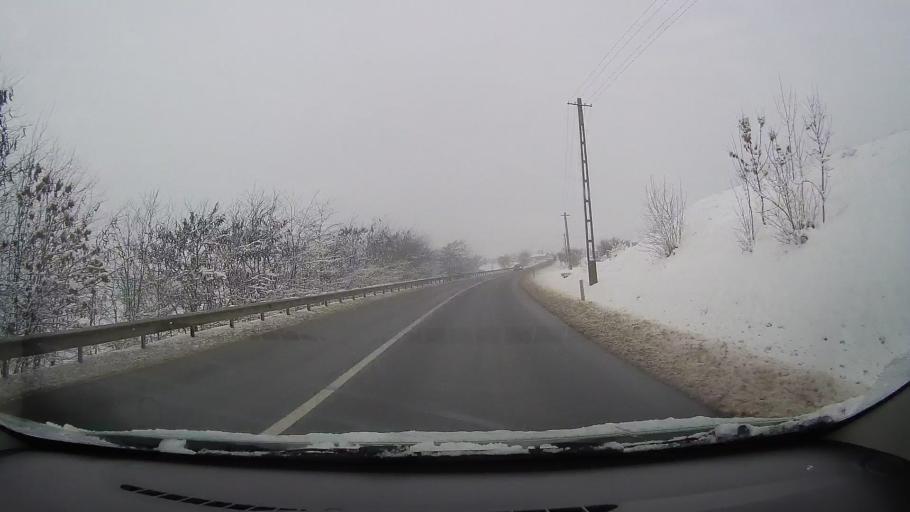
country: RO
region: Alba
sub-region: Municipiul Sebes
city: Lancram
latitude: 45.9845
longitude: 23.5121
